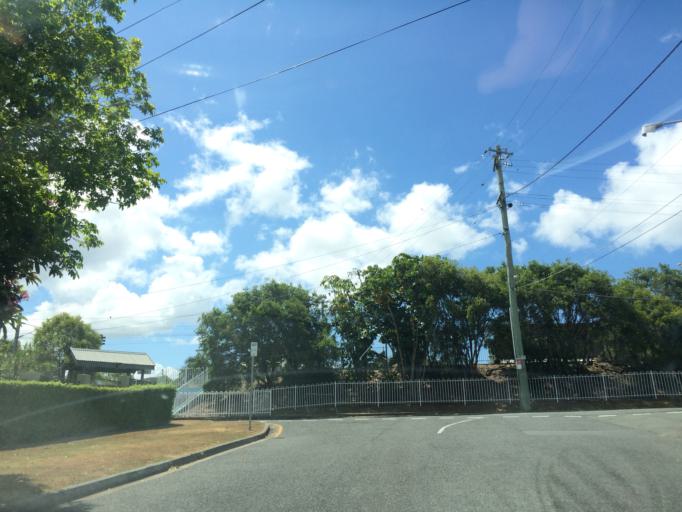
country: AU
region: Queensland
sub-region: Brisbane
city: Seven Hills
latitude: -27.4824
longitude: 153.0619
